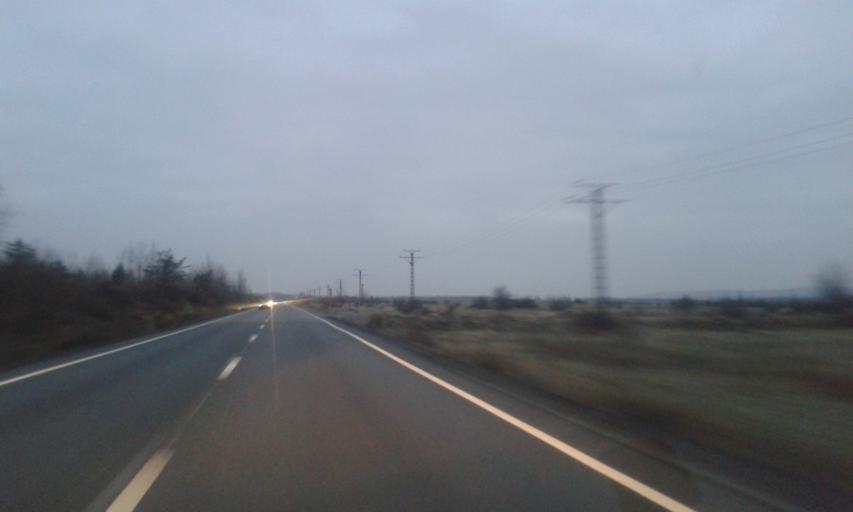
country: RO
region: Gorj
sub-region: Comuna Bumbesti-Jiu
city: Bumbesti-Jiu
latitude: 45.1493
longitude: 23.3718
